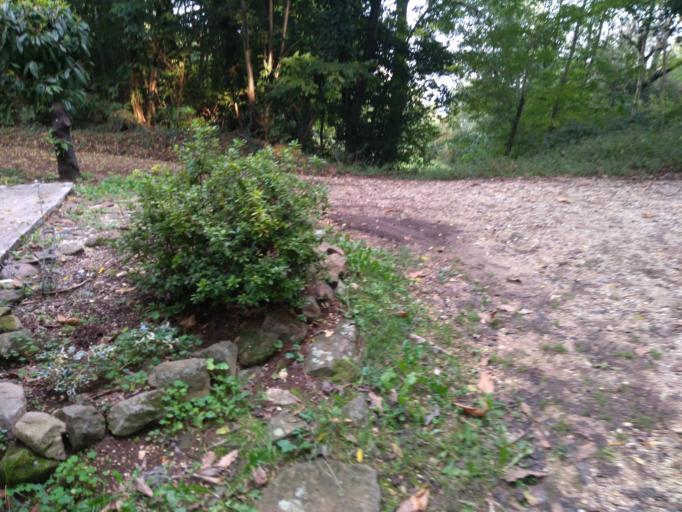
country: IT
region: Veneto
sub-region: Provincia di Vicenza
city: Monte di Malo
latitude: 45.6684
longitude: 11.3501
